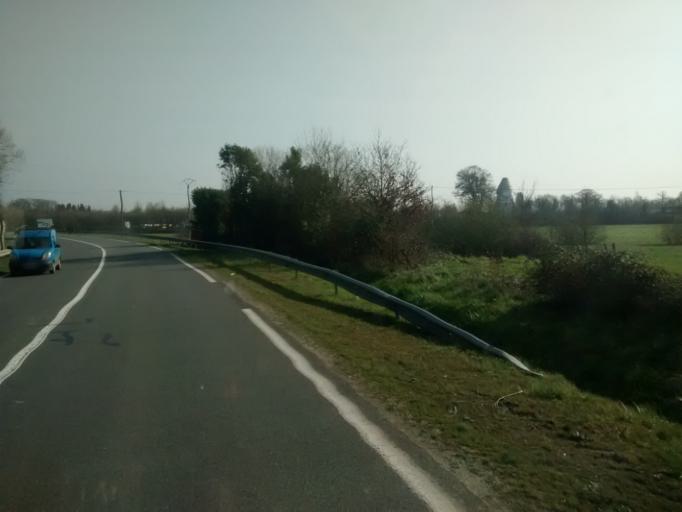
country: FR
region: Brittany
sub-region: Departement d'Ille-et-Vilaine
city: Chavagne
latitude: 48.0624
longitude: -1.7798
